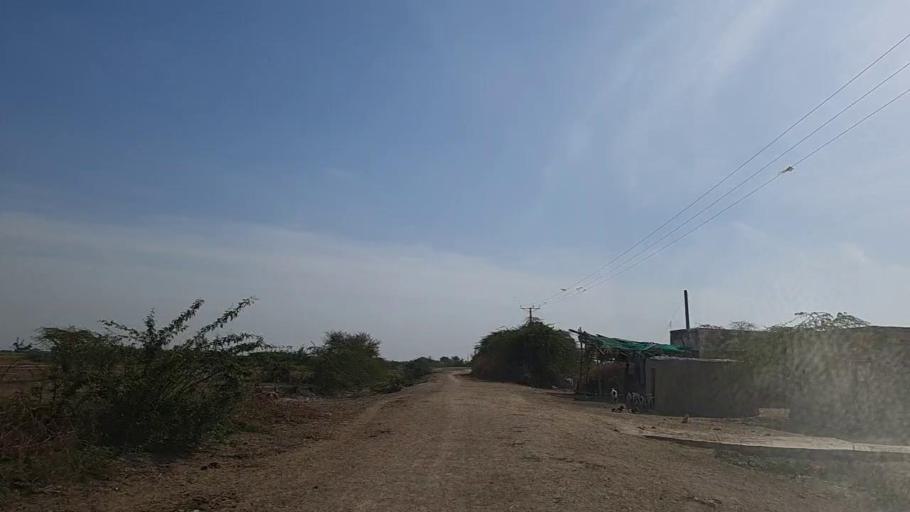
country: PK
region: Sindh
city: Samaro
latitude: 25.2061
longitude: 69.4361
